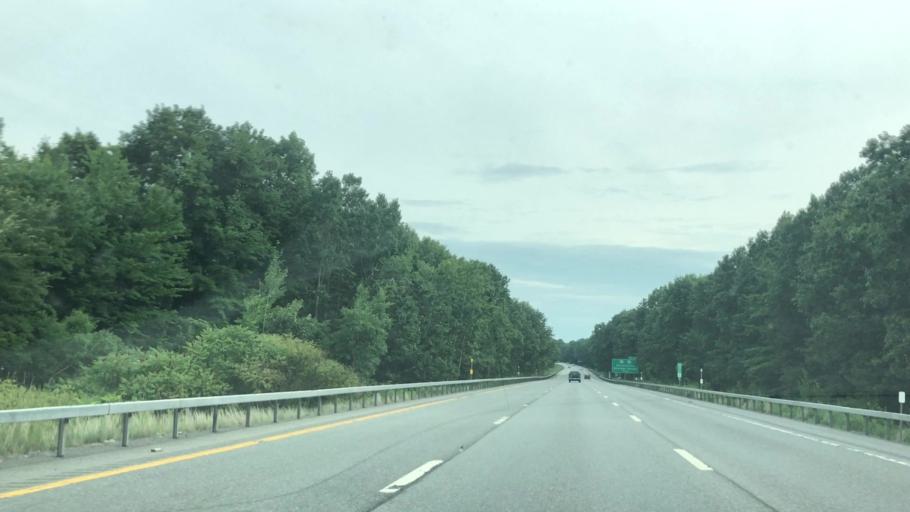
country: US
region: New York
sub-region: Saratoga County
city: Saratoga Springs
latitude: 43.1159
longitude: -73.7467
